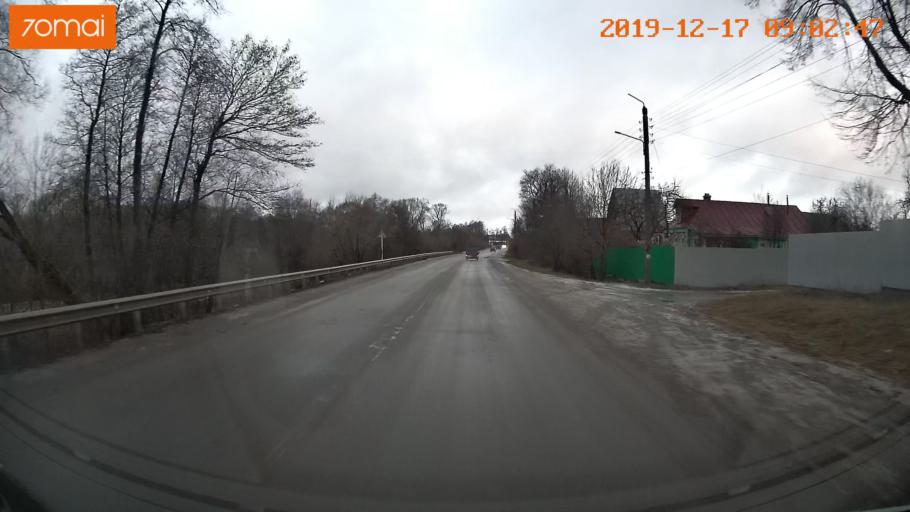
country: RU
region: Vladimir
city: Kosterevo
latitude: 55.9526
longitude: 39.6332
